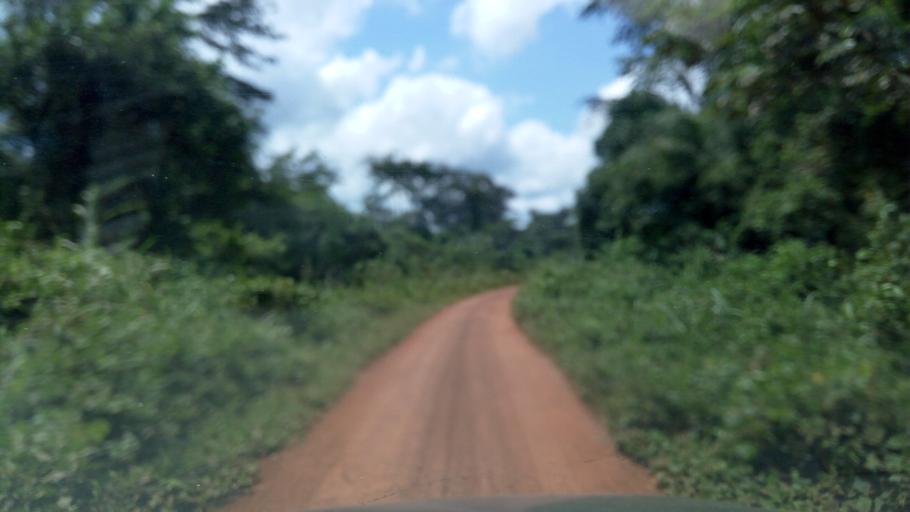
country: CF
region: Bangui
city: Bangui
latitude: 4.0366
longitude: 18.7496
